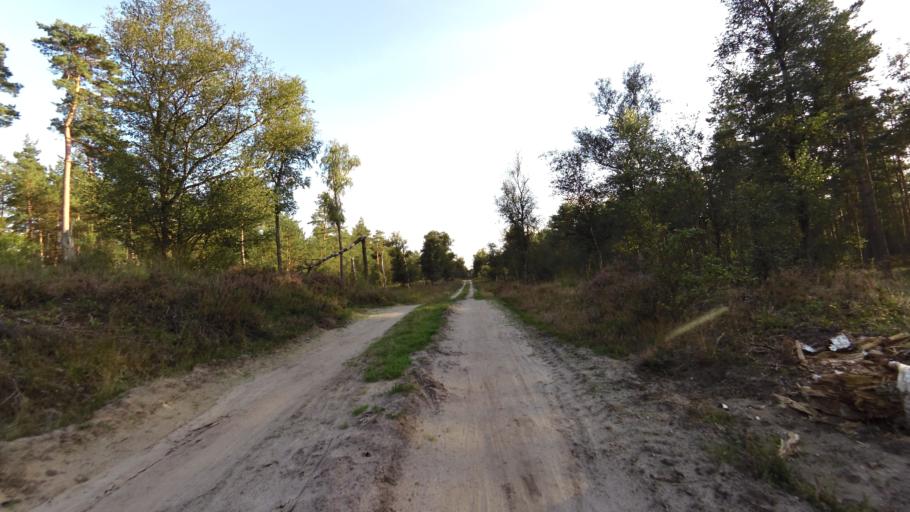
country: NL
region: Gelderland
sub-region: Gemeente Epe
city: Vaassen
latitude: 52.2817
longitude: 5.8766
